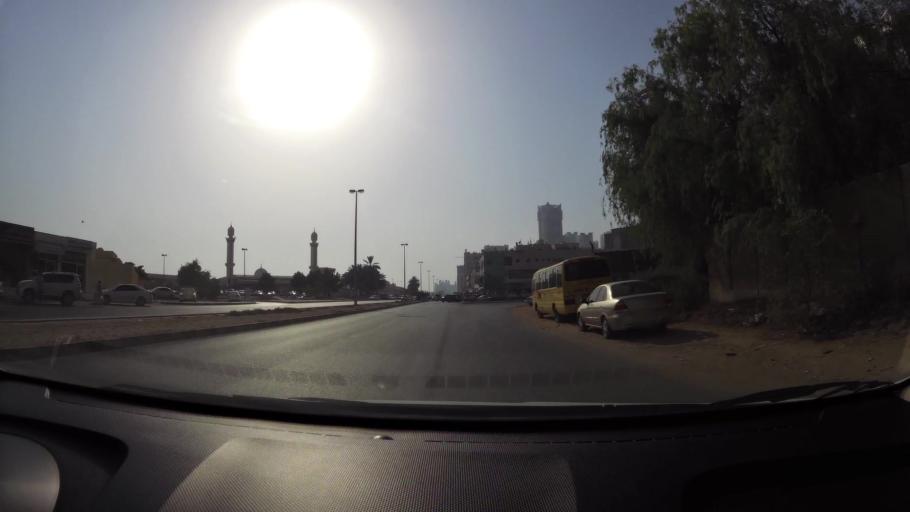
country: AE
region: Ajman
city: Ajman
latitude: 25.3881
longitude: 55.4370
